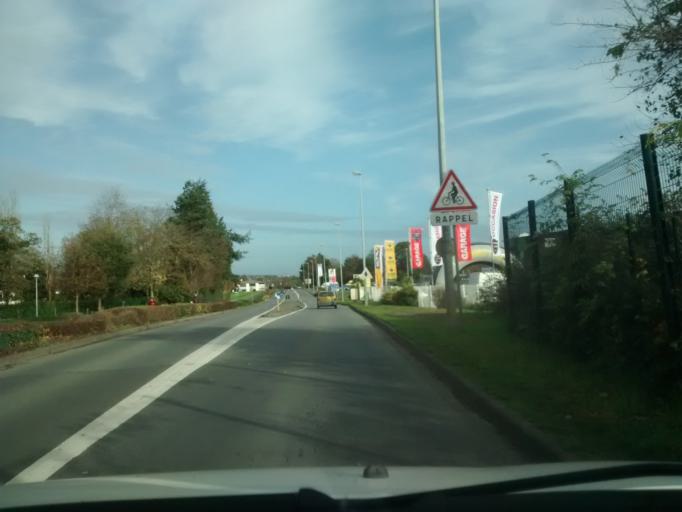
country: FR
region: Brittany
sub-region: Departement d'Ille-et-Vilaine
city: Noyal-sur-Vilaine
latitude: 48.1193
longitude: -1.5318
